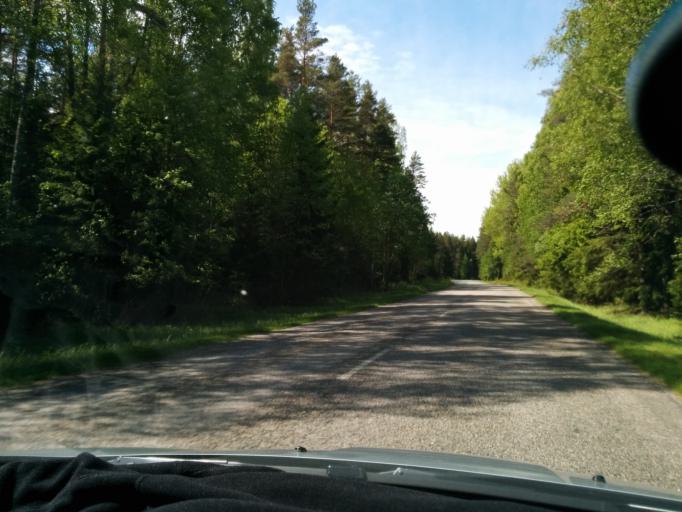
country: EE
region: Laeaene-Virumaa
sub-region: Kadrina vald
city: Kadrina
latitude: 59.5443
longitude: 26.0253
